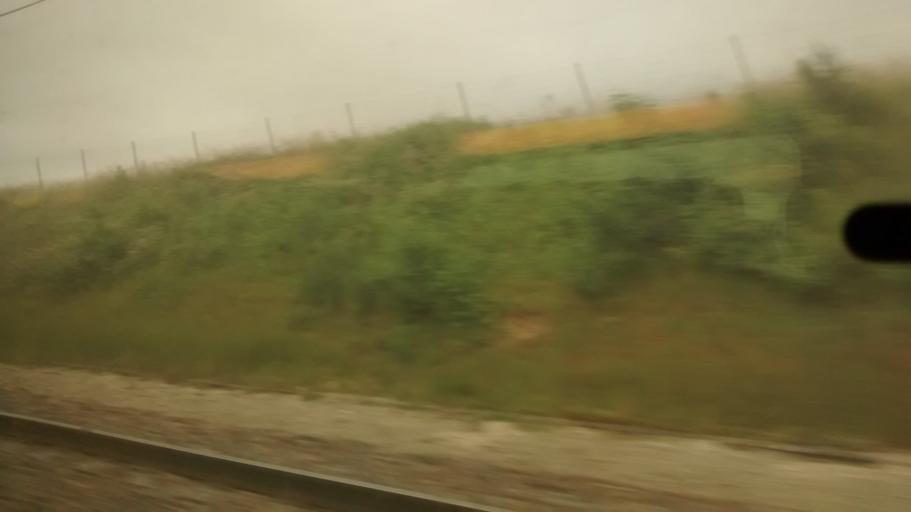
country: FR
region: Bourgogne
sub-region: Departement de l'Yonne
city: Courlon-sur-Yonne
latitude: 48.3568
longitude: 3.1661
